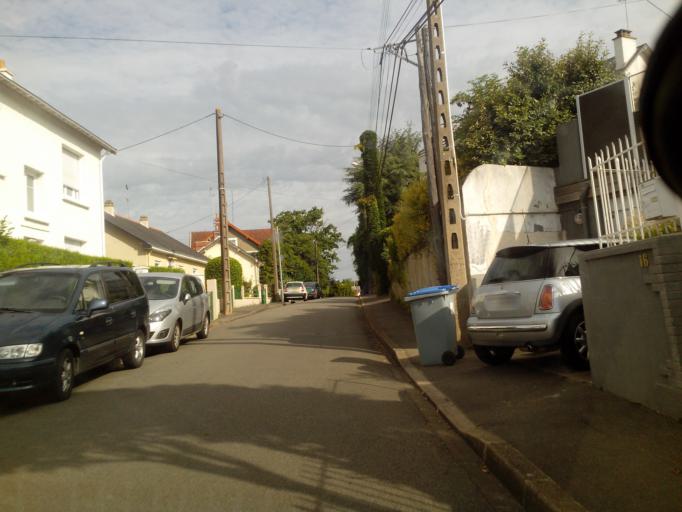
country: FR
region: Pays de la Loire
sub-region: Departement de la Loire-Atlantique
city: Nantes
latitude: 47.2508
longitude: -1.5783
